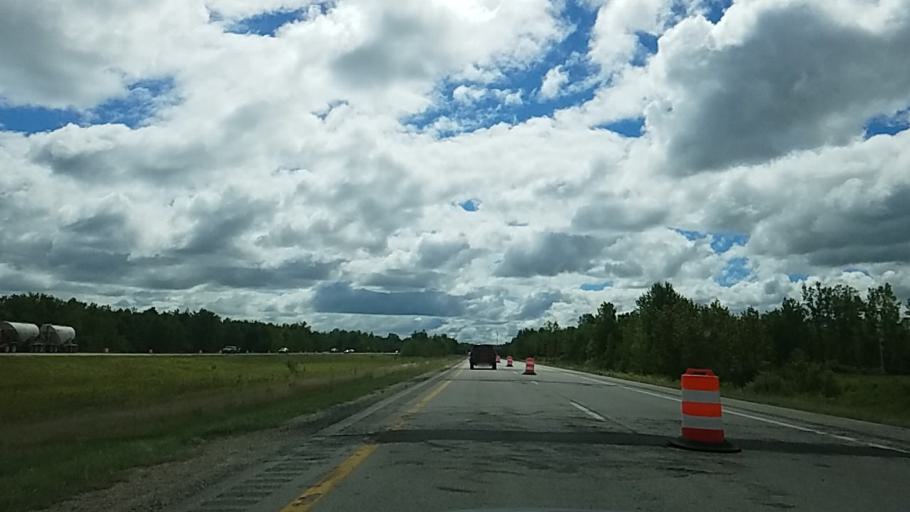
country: US
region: Michigan
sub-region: Arenac County
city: Standish
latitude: 43.9560
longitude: -84.0158
